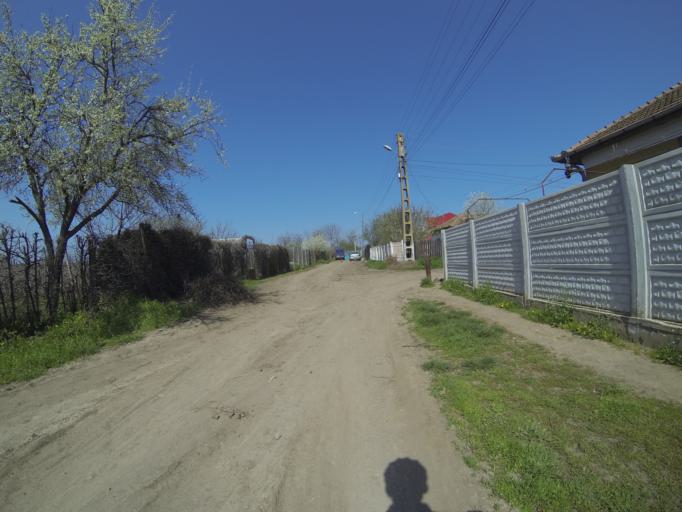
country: RO
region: Dolj
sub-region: Comuna Segarcea
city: Segarcea
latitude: 44.0927
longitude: 23.7320
